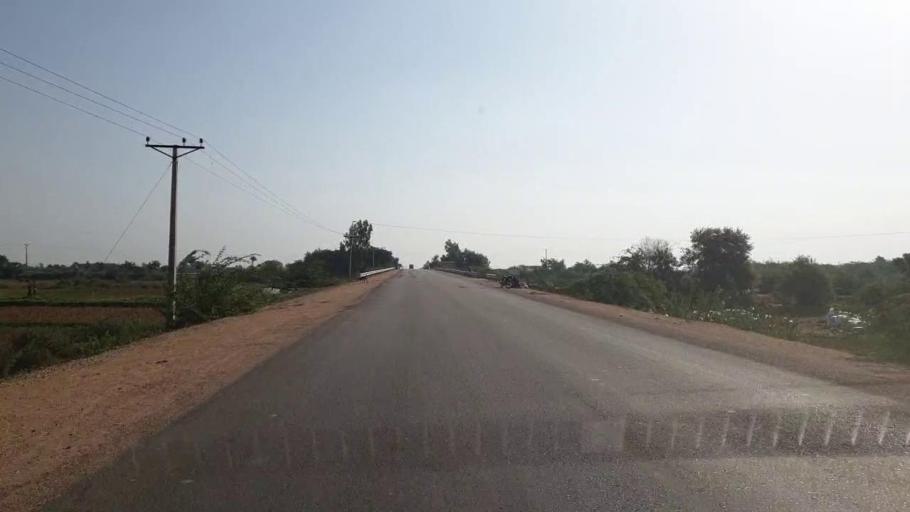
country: PK
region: Sindh
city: Tando Bago
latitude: 24.6580
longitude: 68.9708
